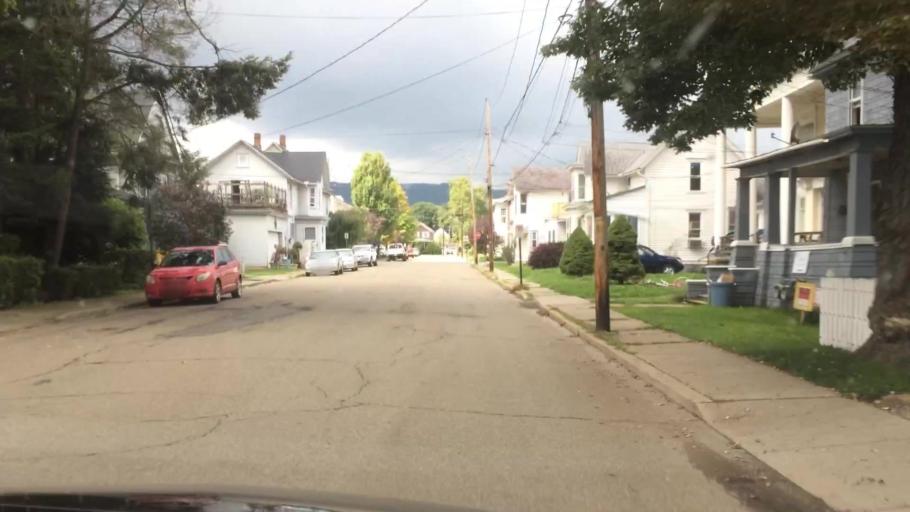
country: US
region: Pennsylvania
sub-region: McKean County
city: Bradford
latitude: 41.9580
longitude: -78.6463
